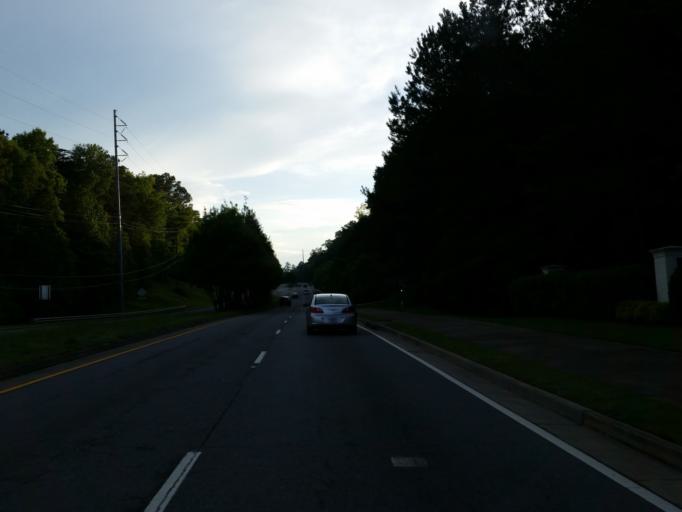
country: US
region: Georgia
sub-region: Fulton County
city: Roswell
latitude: 34.0108
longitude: -84.3777
